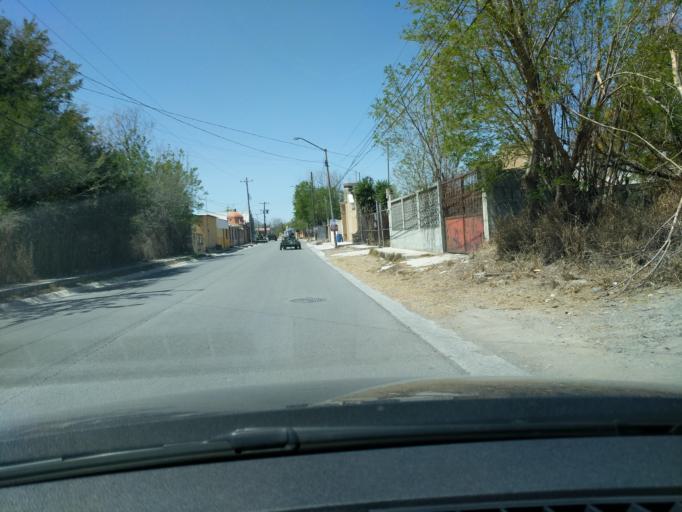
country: MX
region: Nuevo Leon
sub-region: Apodaca
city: Artemio Trevino
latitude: 25.8127
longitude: -100.1423
